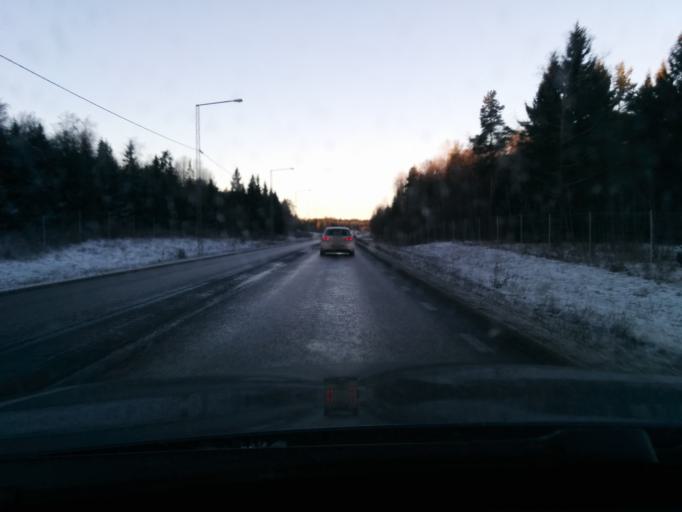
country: SE
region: Stockholm
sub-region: Taby Kommun
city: Taby
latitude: 59.4834
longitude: 18.1155
